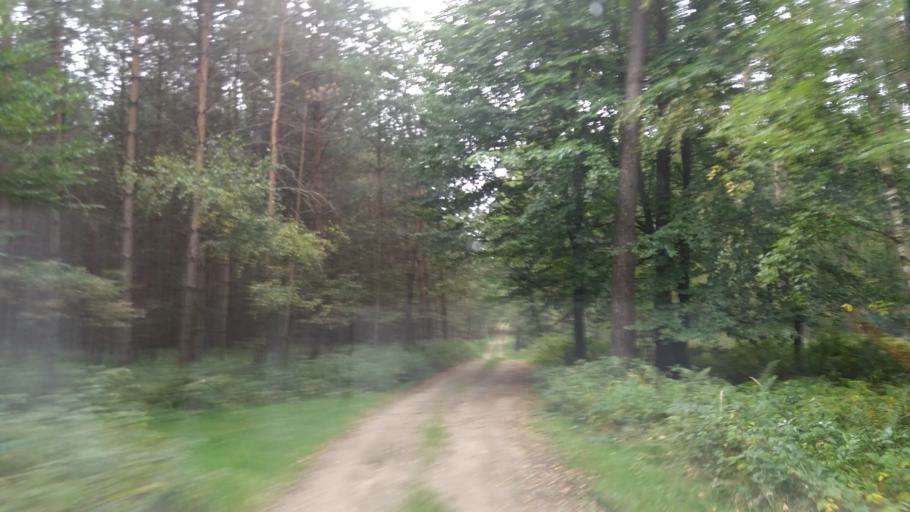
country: PL
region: West Pomeranian Voivodeship
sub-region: Powiat choszczenski
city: Bierzwnik
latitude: 52.9852
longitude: 15.5865
